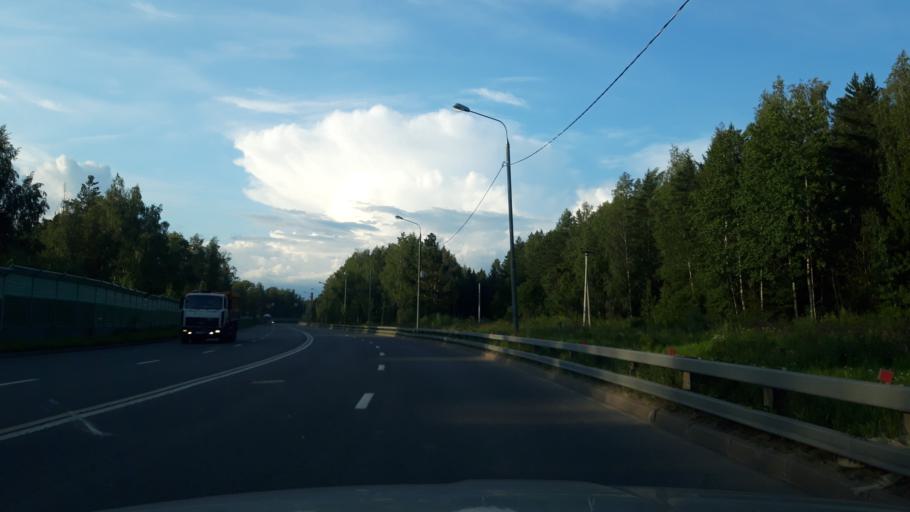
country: RU
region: Moskovskaya
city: Alabushevo
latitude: 55.9992
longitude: 37.1623
